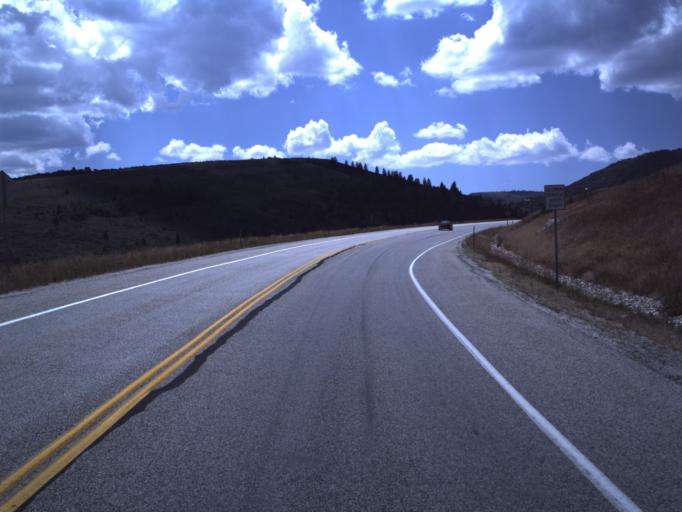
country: US
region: Idaho
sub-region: Bear Lake County
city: Paris
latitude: 41.9363
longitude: -111.4119
